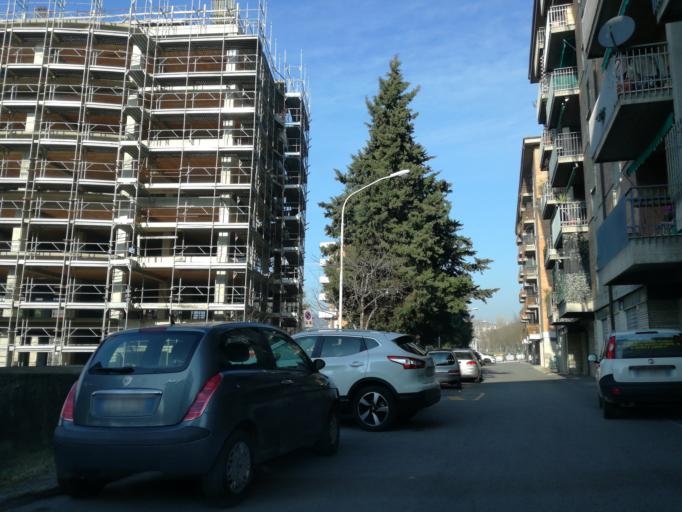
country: IT
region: Umbria
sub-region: Provincia di Perugia
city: Perugia
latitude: 43.1089
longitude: 12.3673
